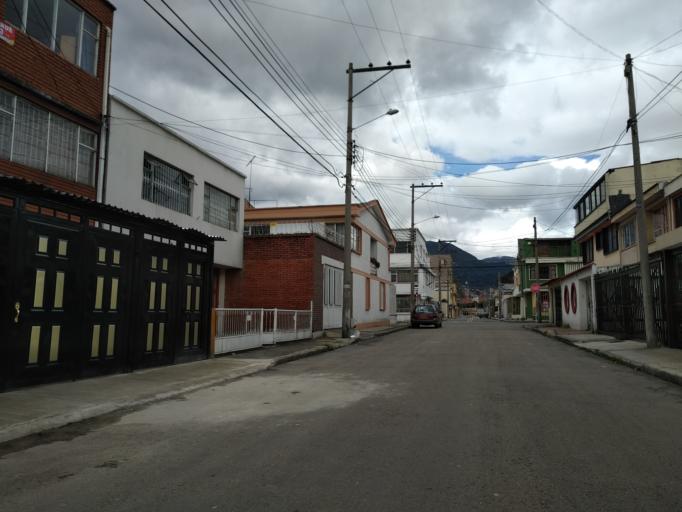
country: CO
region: Bogota D.C.
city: Bogota
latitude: 4.5965
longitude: -74.1005
